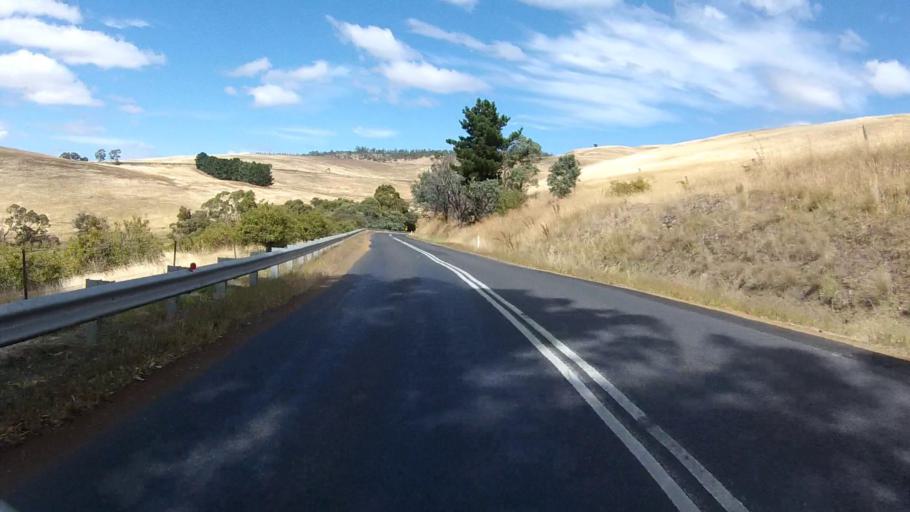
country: AU
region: Tasmania
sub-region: Brighton
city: Bridgewater
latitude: -42.5676
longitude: 147.3893
